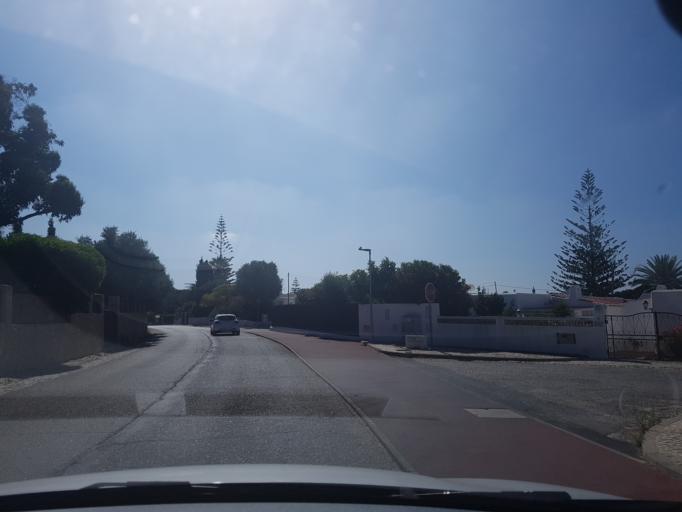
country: PT
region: Faro
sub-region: Lagoa
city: Carvoeiro
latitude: 37.0951
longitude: -8.4629
